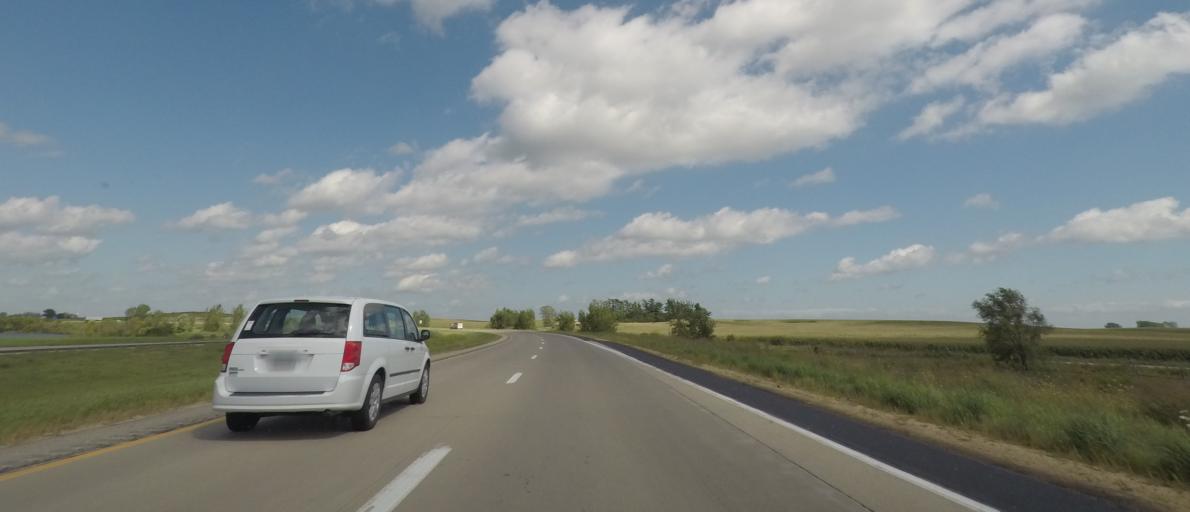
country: US
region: Iowa
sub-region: Jones County
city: Monticello
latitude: 42.2081
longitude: -91.1802
